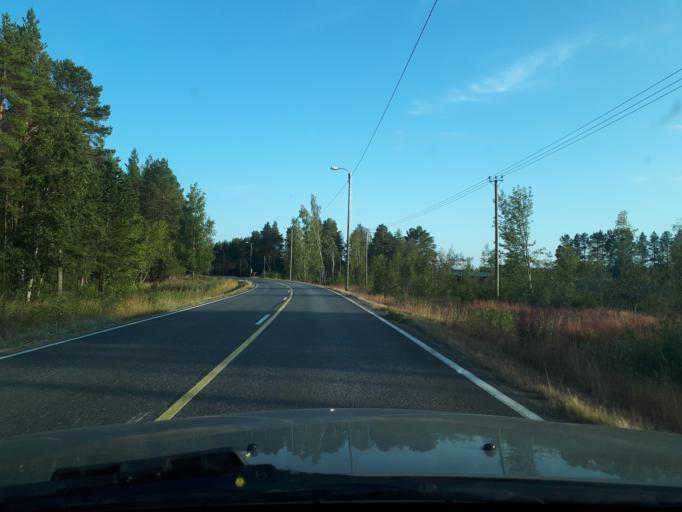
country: FI
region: Northern Ostrobothnia
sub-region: Oulu
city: Oulunsalo
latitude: 64.9894
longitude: 25.2577
